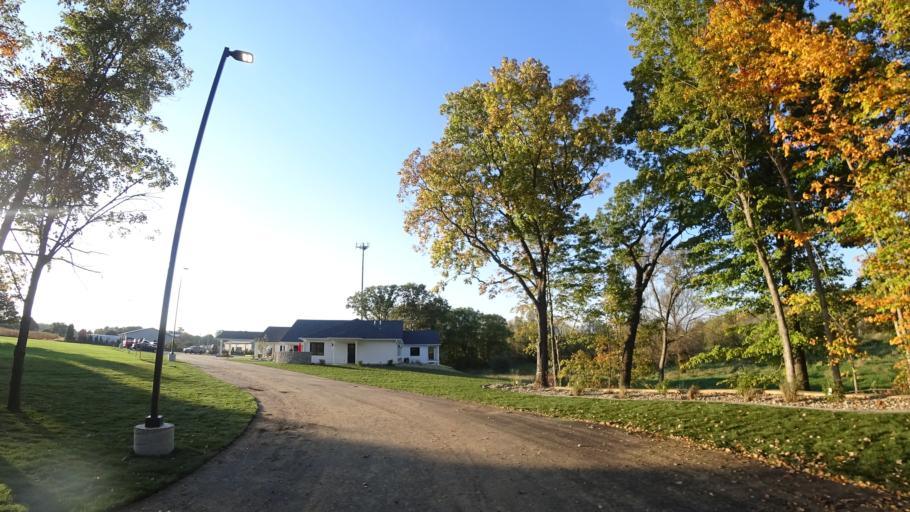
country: US
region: Michigan
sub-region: Saint Joseph County
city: Three Rivers
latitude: 41.9509
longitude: -85.6432
